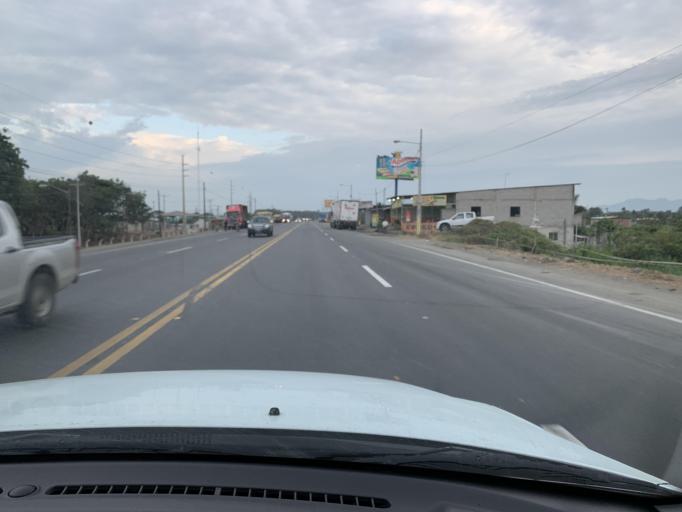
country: EC
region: Guayas
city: Yaguachi Nuevo
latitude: -2.2408
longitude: -79.6380
